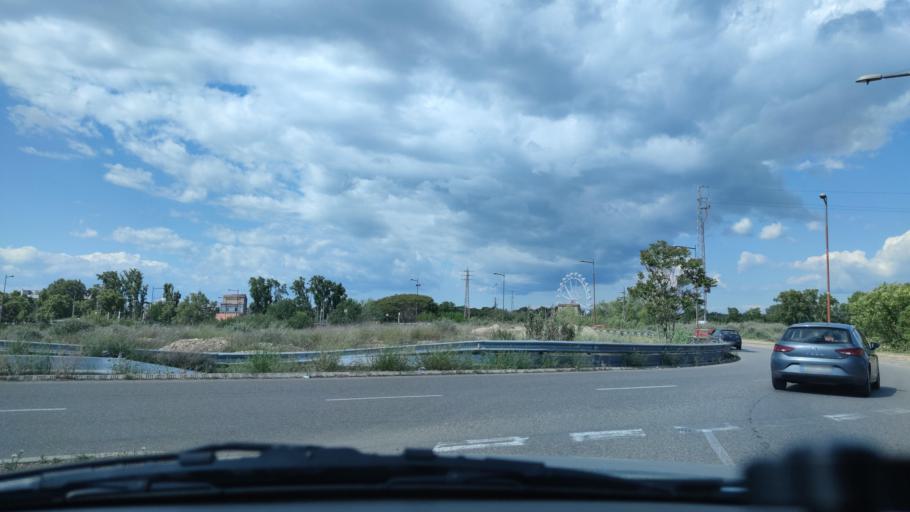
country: ES
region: Catalonia
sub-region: Provincia de Lleida
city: Lleida
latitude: 41.6123
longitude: 0.6395
